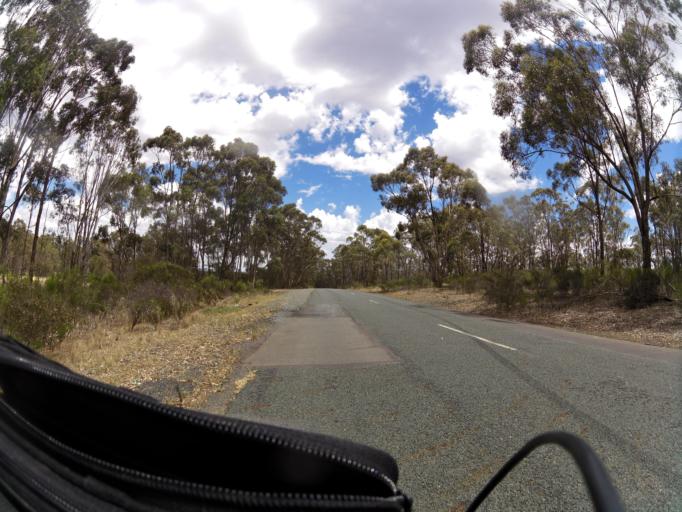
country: AU
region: Victoria
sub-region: Greater Shepparton
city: Shepparton
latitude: -36.6845
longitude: 145.1841
